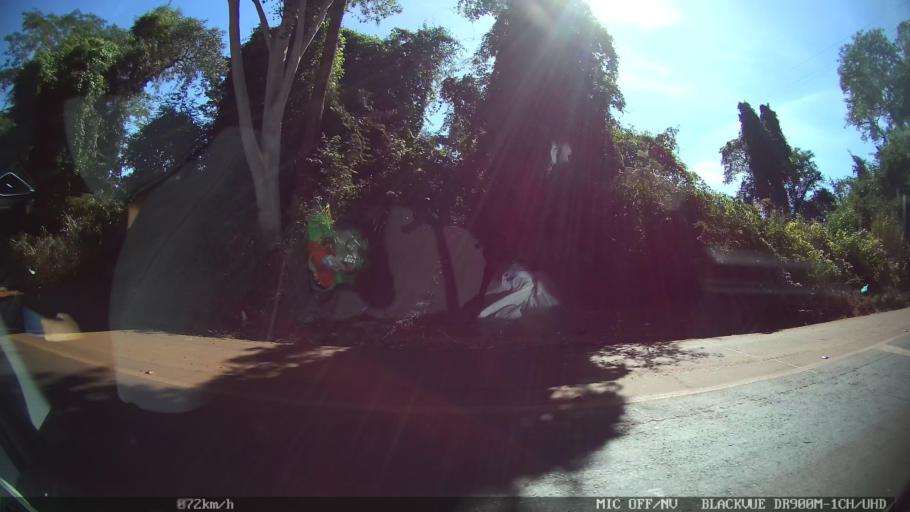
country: BR
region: Sao Paulo
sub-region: Barretos
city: Barretos
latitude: -20.4493
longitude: -48.4529
